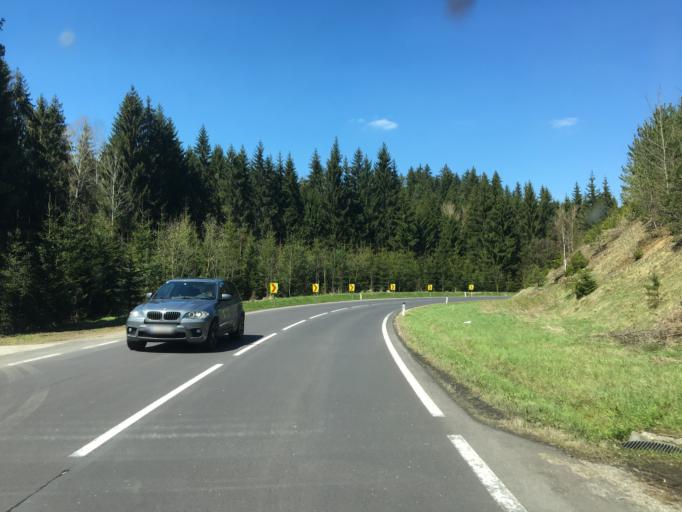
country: AT
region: Upper Austria
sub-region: Politischer Bezirk Urfahr-Umgebung
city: Sonnberg im Muehlkreis
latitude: 48.4885
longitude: 14.2965
